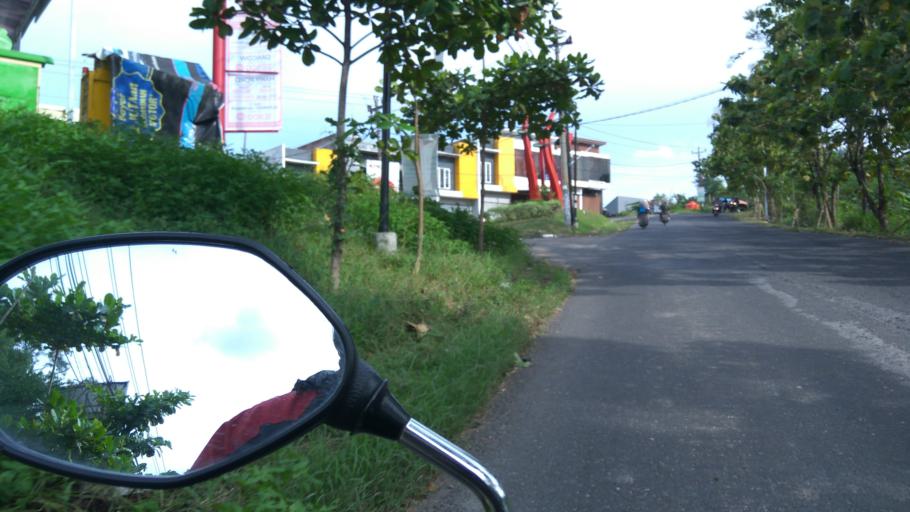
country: ID
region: Central Java
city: Mranggen
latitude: -7.0409
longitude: 110.4606
